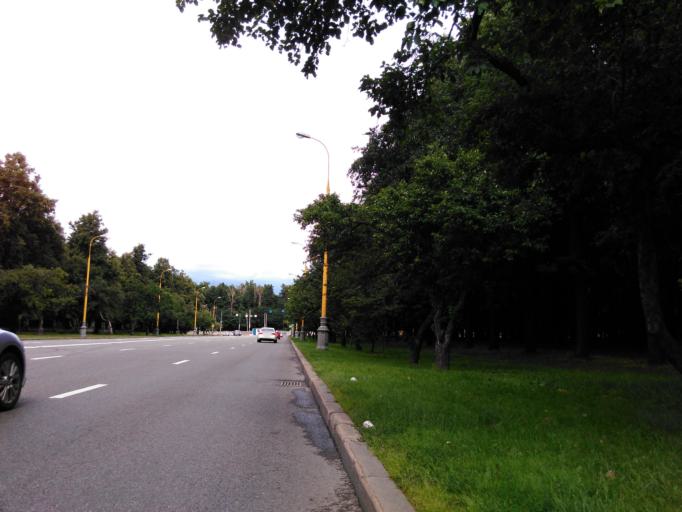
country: RU
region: Moscow
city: Vorob'yovo
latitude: 55.7064
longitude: 37.5307
